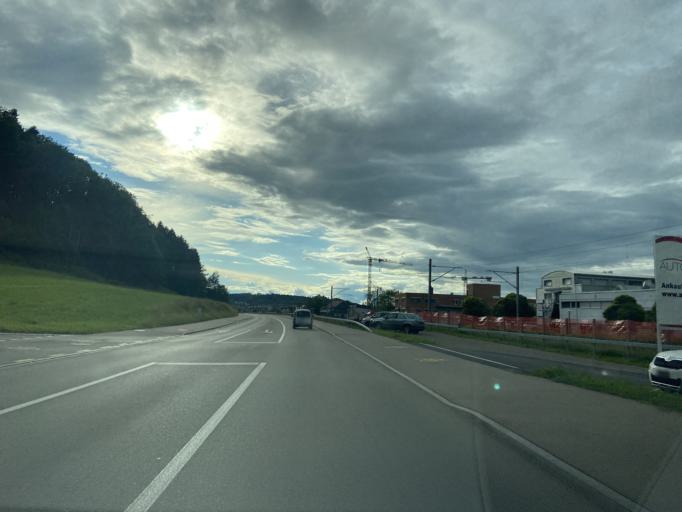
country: CH
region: Zurich
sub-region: Bezirk Winterthur
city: Elsau-Raeterschen / Raeterschen
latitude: 47.5008
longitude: 8.7857
